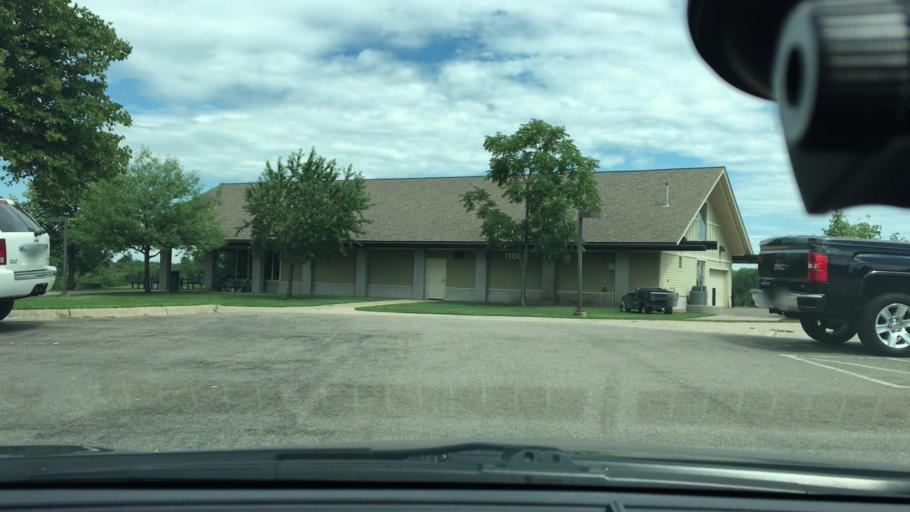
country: US
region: Minnesota
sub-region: Hennepin County
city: New Hope
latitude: 45.0600
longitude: -93.4181
